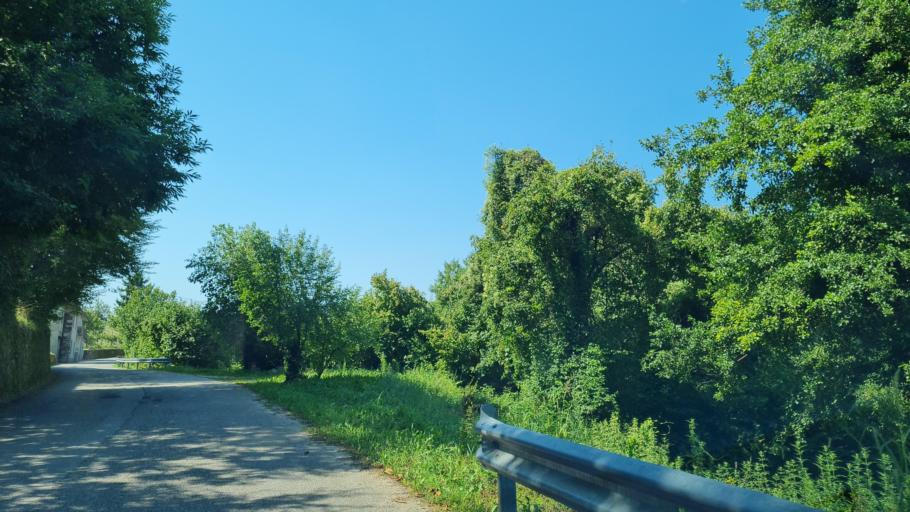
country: IT
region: Veneto
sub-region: Provincia di Vicenza
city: Salcedo
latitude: 45.7543
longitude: 11.5910
